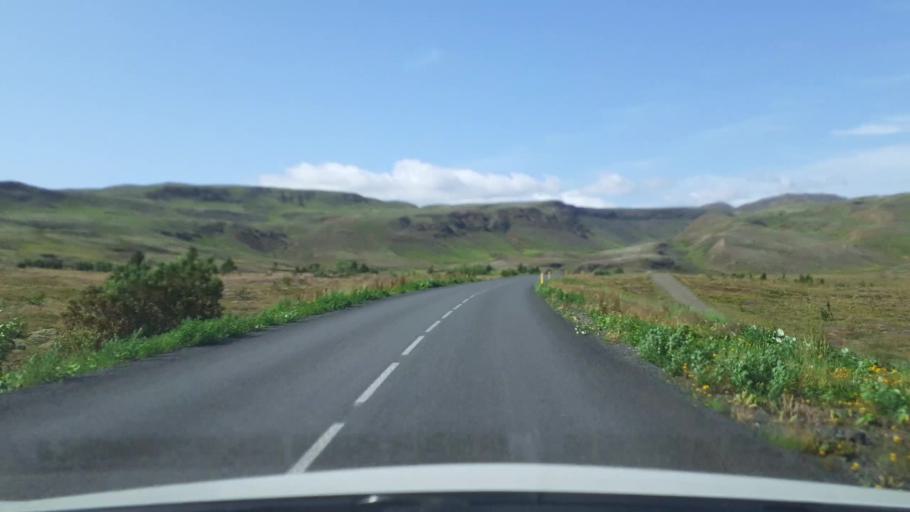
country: IS
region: South
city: Hveragerdi
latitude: 64.0148
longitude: -21.2092
